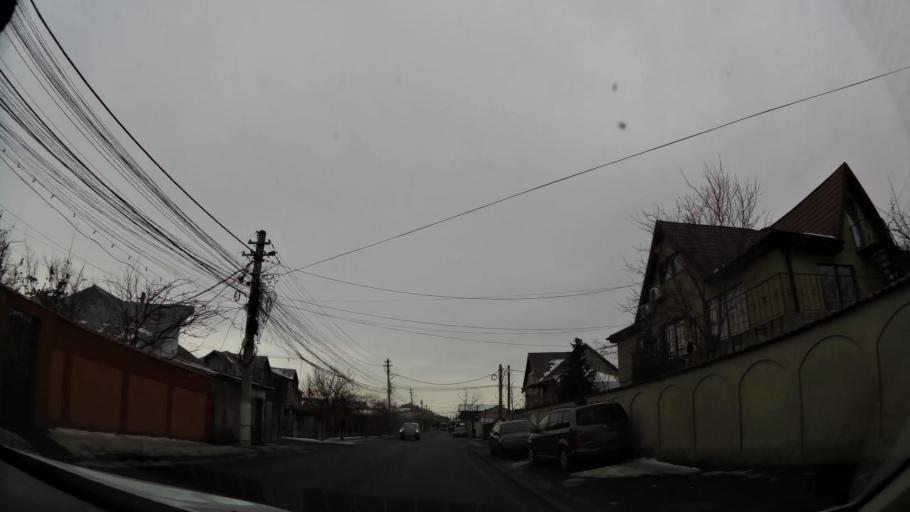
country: RO
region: Ilfov
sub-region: Comuna Pantelimon
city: Pantelimon
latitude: 44.4580
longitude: 26.2094
